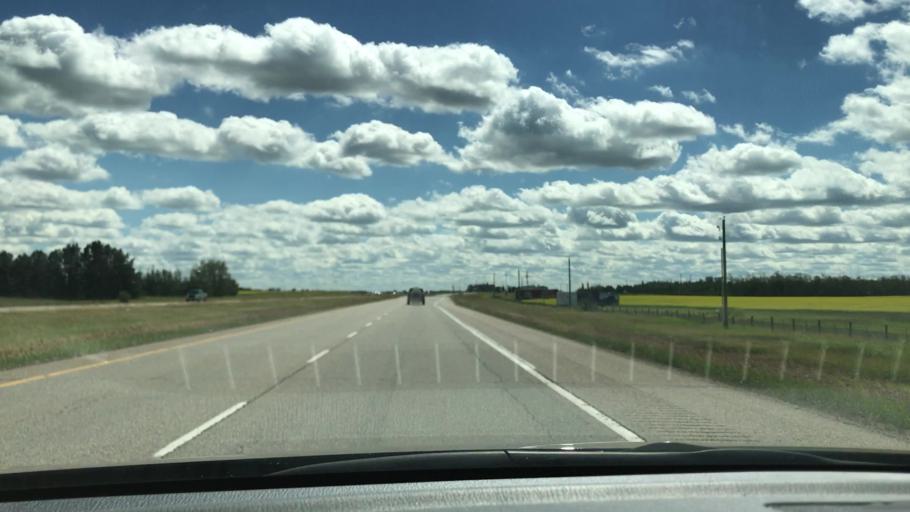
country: CA
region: Alberta
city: Leduc
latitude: 53.2386
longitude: -113.5657
